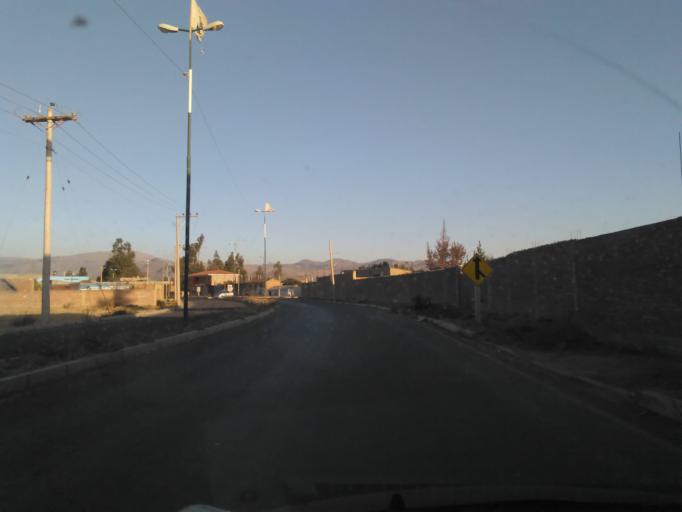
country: BO
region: Cochabamba
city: Punata
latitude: -17.5479
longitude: -65.8255
